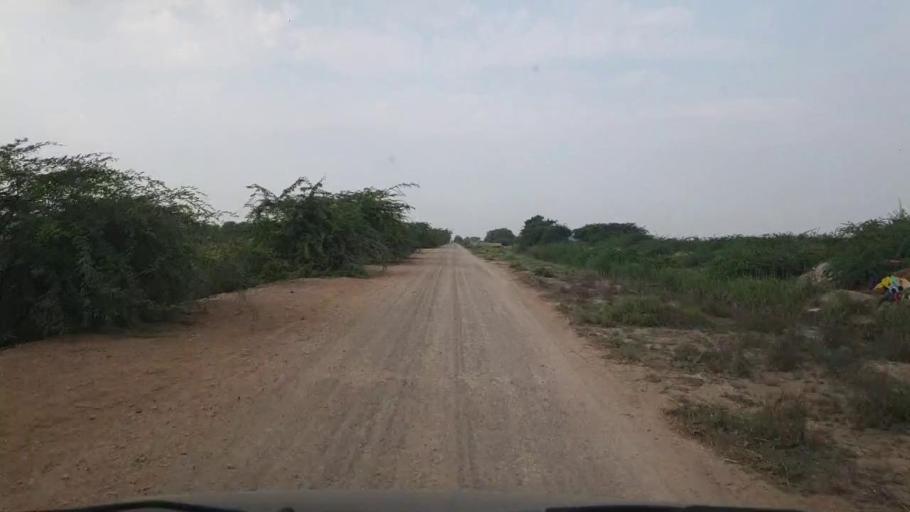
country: PK
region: Sindh
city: Kario
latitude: 24.6031
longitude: 68.6001
